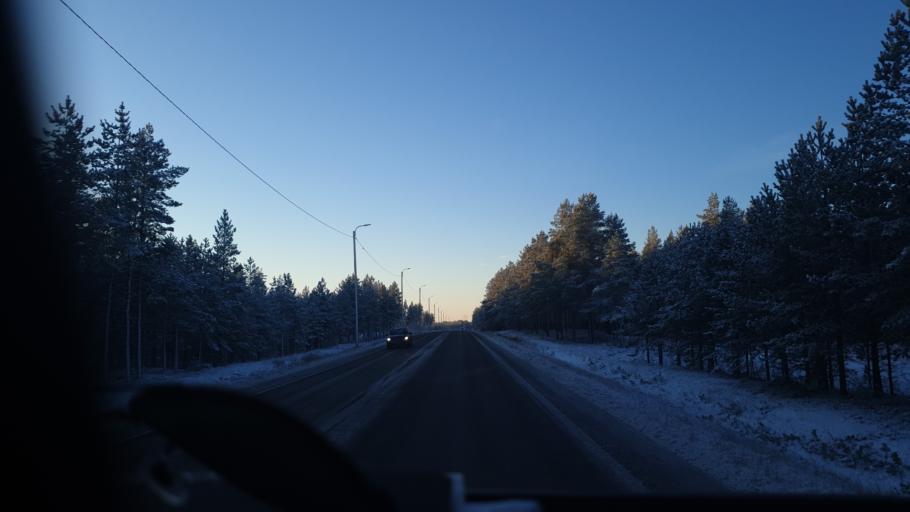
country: FI
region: Northern Ostrobothnia
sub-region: Ylivieska
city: Kalajoki
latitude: 64.2359
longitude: 23.8306
